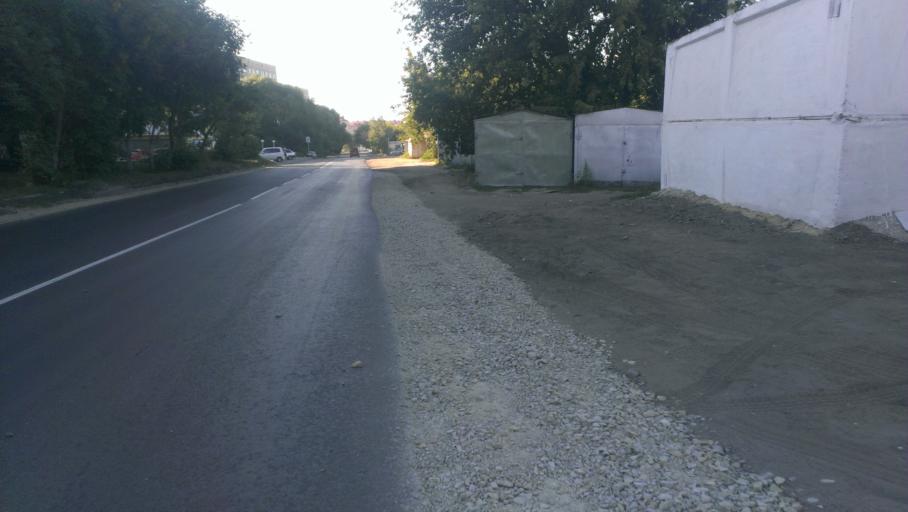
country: RU
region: Altai Krai
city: Novosilikatnyy
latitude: 53.3055
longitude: 83.6264
